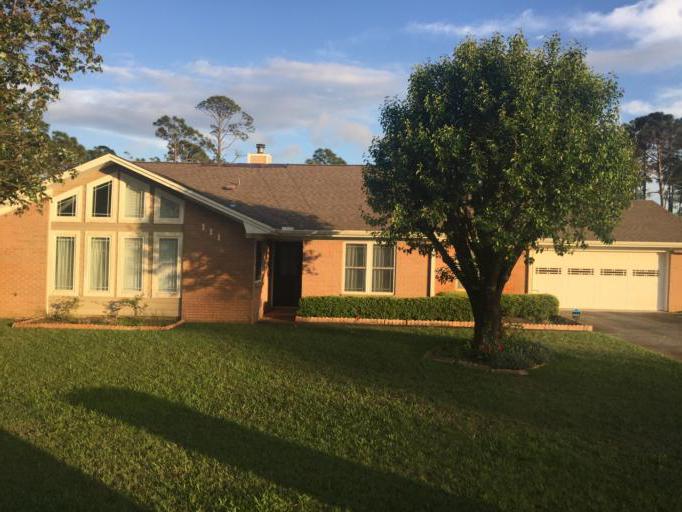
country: US
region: Florida
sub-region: Bay County
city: Panama City Beach
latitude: 30.2255
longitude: -85.8430
